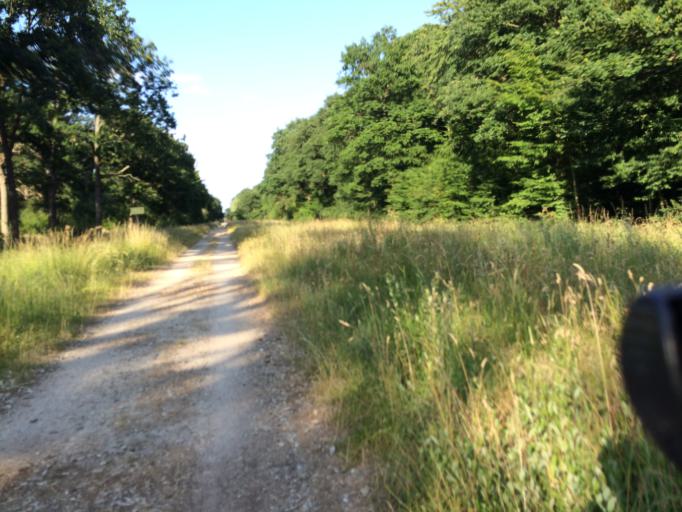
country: FR
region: Ile-de-France
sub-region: Departement de l'Essonne
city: Etiolles
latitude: 48.6473
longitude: 2.4823
